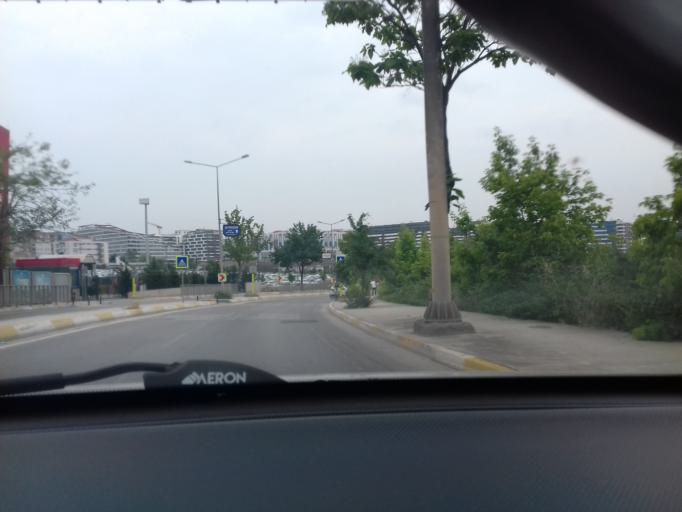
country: TR
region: Istanbul
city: Sultanbeyli
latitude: 40.9221
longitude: 29.3088
